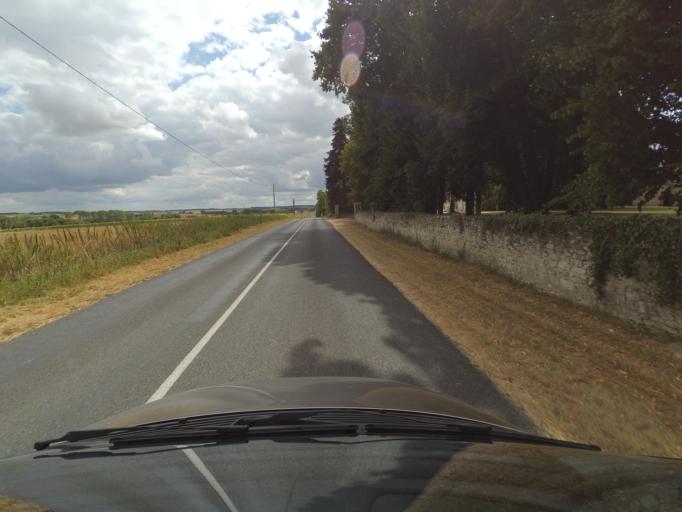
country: FR
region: Poitou-Charentes
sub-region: Departement de la Vienne
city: Saint-Gervais-les-Trois-Clochers
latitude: 46.9586
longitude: 0.3935
